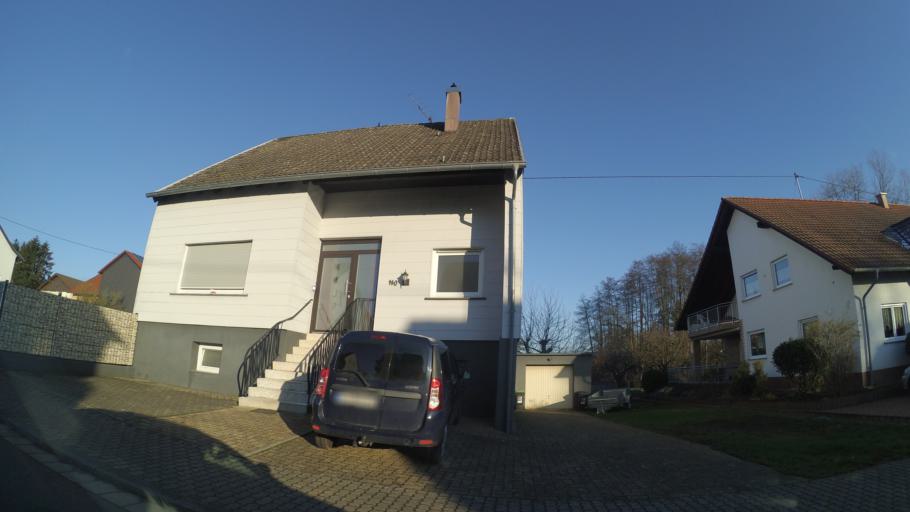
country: DE
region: Saarland
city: Saarwellingen
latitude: 49.3581
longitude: 6.8644
